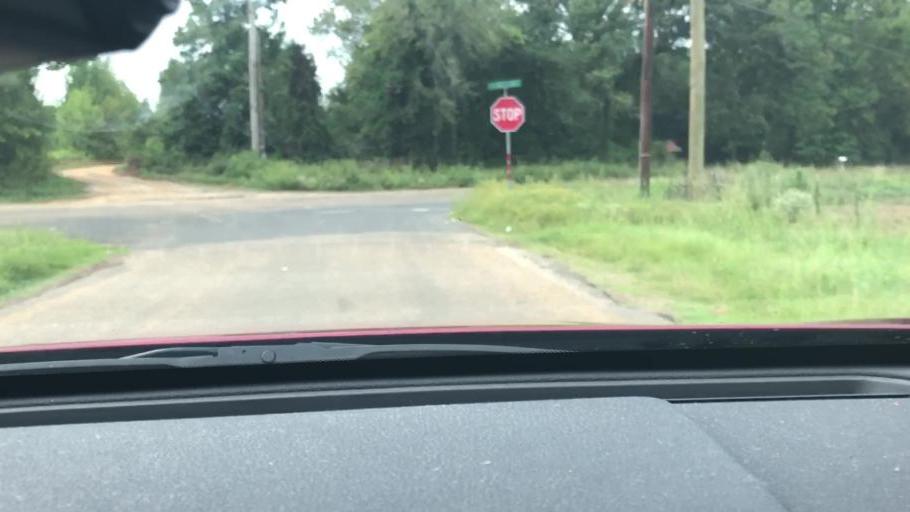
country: US
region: Texas
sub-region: Bowie County
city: Wake Village
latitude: 33.3759
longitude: -94.0992
